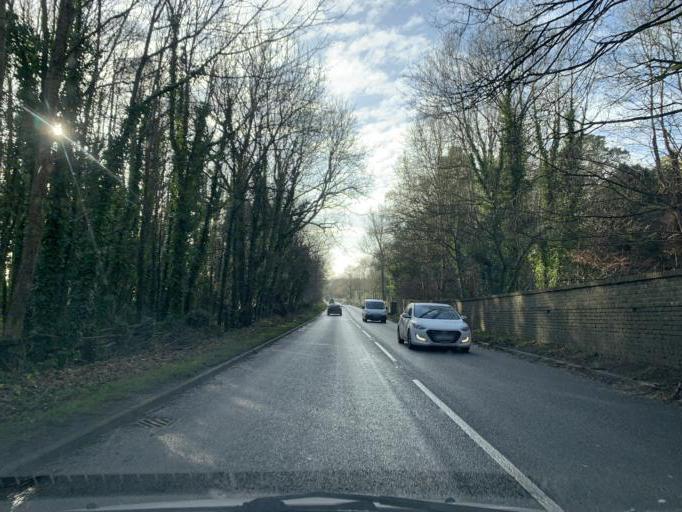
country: GB
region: England
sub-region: Wiltshire
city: Wilton
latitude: 51.0761
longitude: -1.8497
